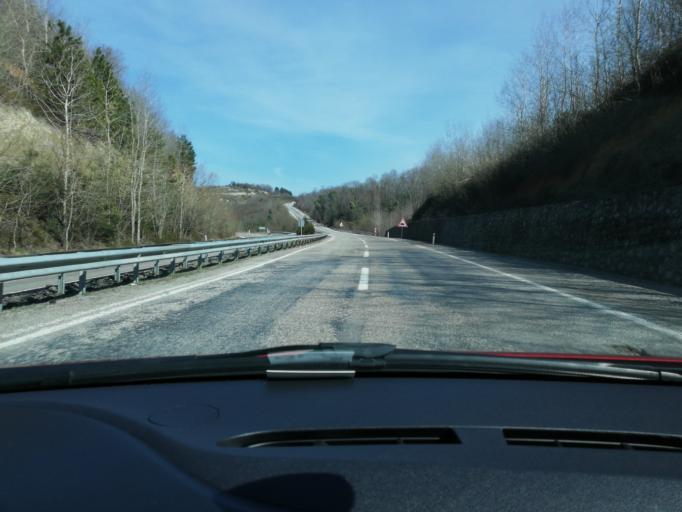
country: TR
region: Bartin
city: Amasra
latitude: 41.7229
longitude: 32.4018
